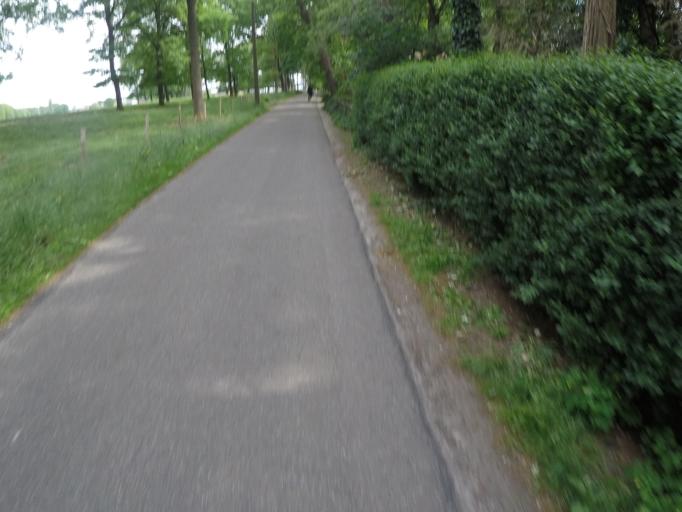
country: BE
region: Flanders
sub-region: Provincie Antwerpen
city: Zoersel
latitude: 51.2928
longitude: 4.6702
